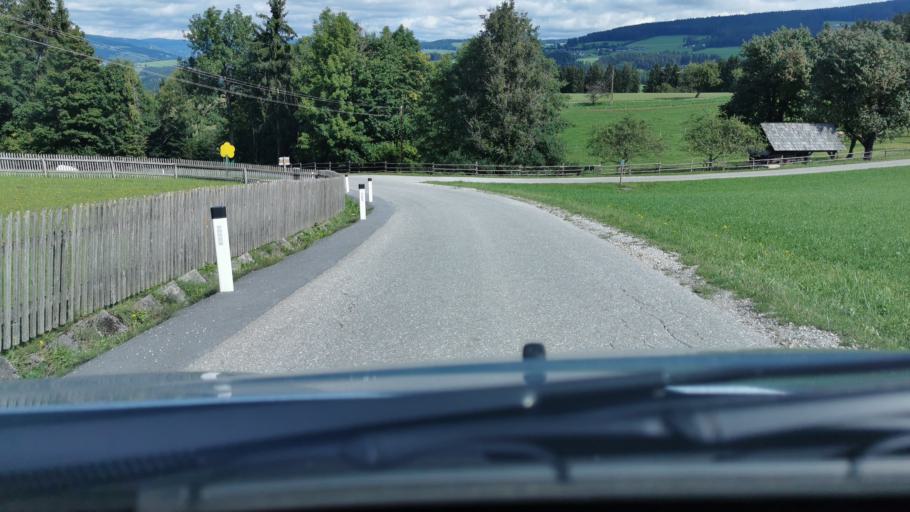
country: AT
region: Styria
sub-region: Politischer Bezirk Weiz
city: Gschaid bei Birkfeld
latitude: 47.3333
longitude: 15.7084
